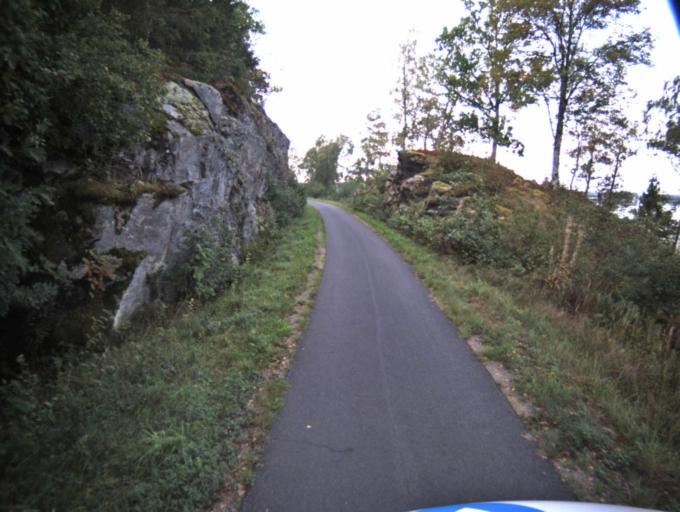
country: SE
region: Vaestra Goetaland
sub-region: Ulricehamns Kommun
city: Ulricehamn
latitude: 57.7044
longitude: 13.3947
